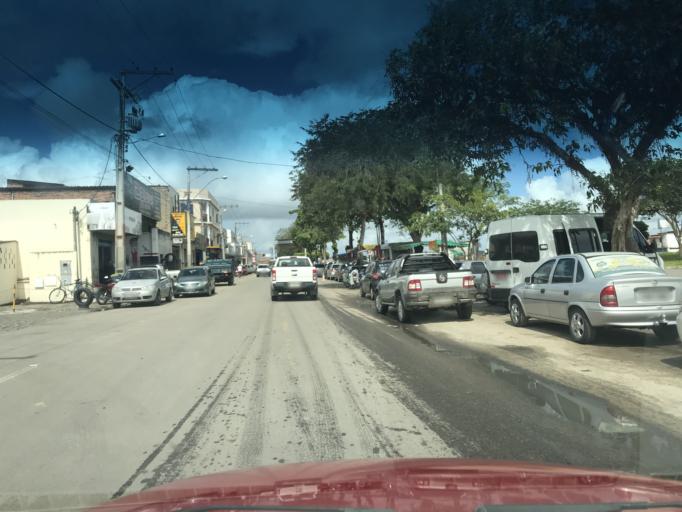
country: BR
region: Bahia
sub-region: Santo Antonio De Jesus
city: Santo Antonio de Jesus
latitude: -12.9646
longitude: -39.2718
